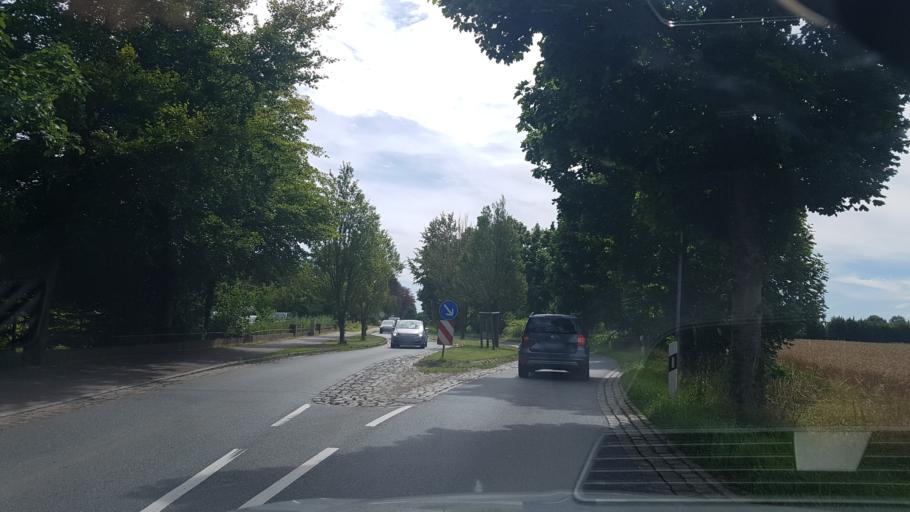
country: DE
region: Schleswig-Holstein
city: Gross Buchwald
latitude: 54.1640
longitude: 10.0787
